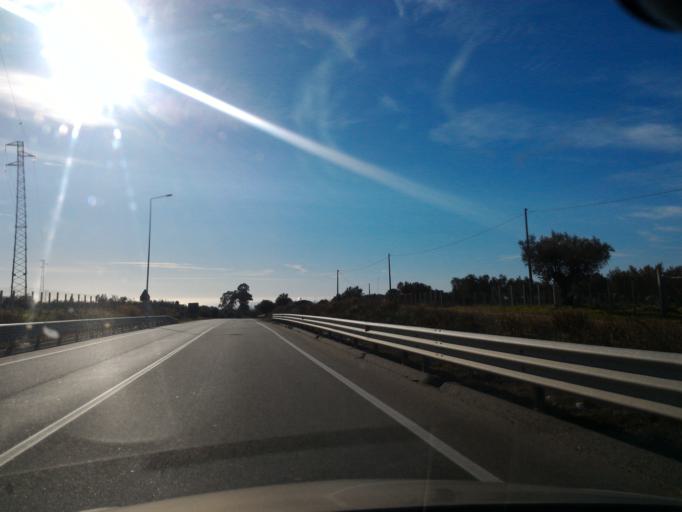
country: IT
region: Calabria
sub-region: Provincia di Crotone
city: Isola di Capo Rizzuto
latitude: 38.9670
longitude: 17.0815
